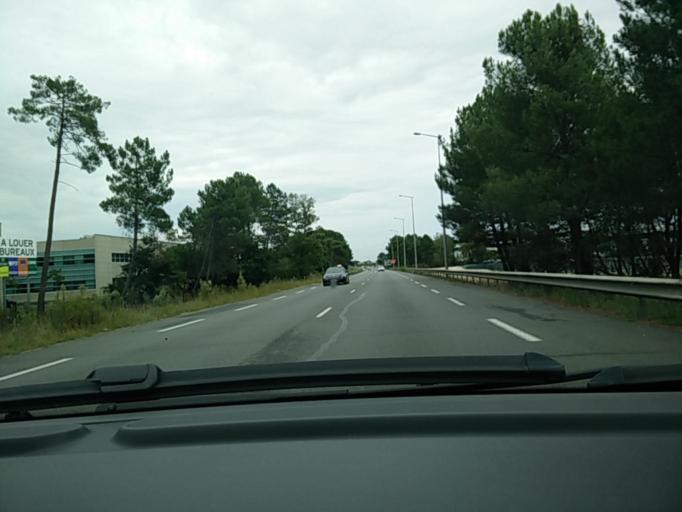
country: FR
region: Aquitaine
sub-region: Departement de la Gironde
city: Le Haillan
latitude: 44.8332
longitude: -0.6866
